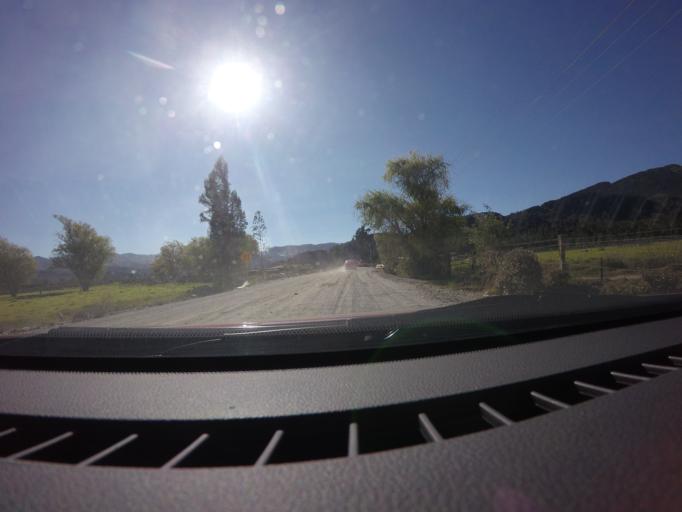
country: CO
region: Cundinamarca
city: Cucunuba
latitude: 5.2690
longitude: -73.7962
